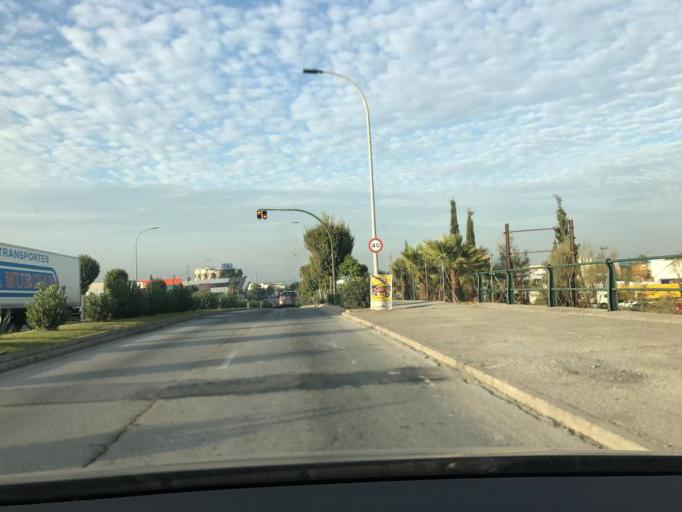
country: ES
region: Andalusia
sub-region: Provincia de Granada
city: Peligros
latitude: 37.2277
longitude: -3.6390
